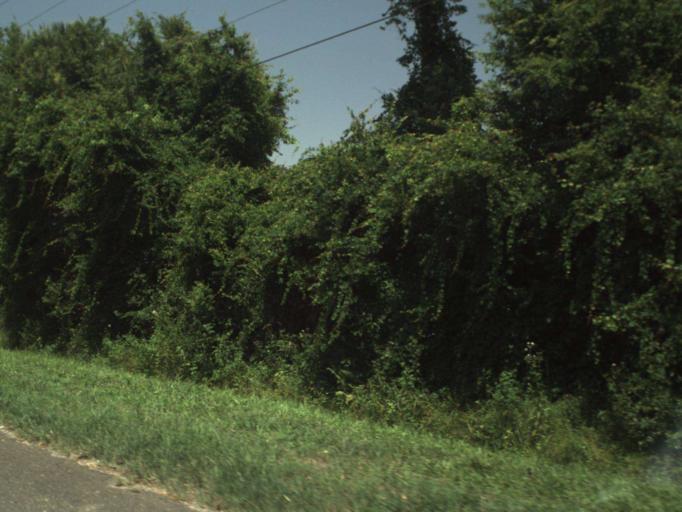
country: US
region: Florida
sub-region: Seminole County
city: Winter Springs
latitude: 28.7264
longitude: -81.3095
